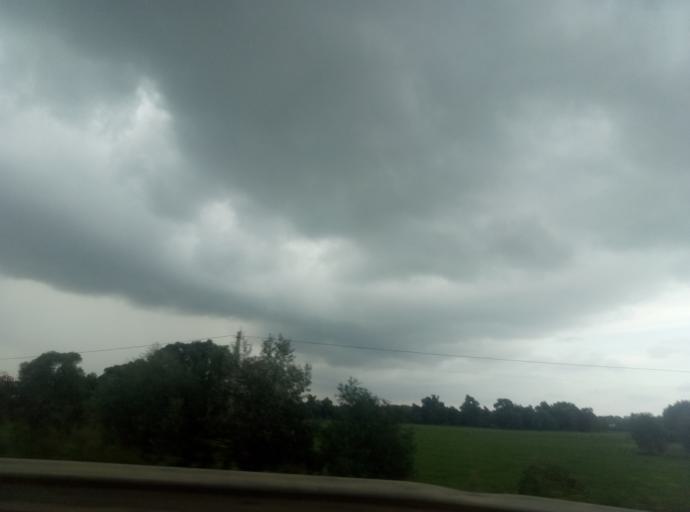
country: RU
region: Tula
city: Kireyevsk
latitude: 53.9731
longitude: 37.9301
